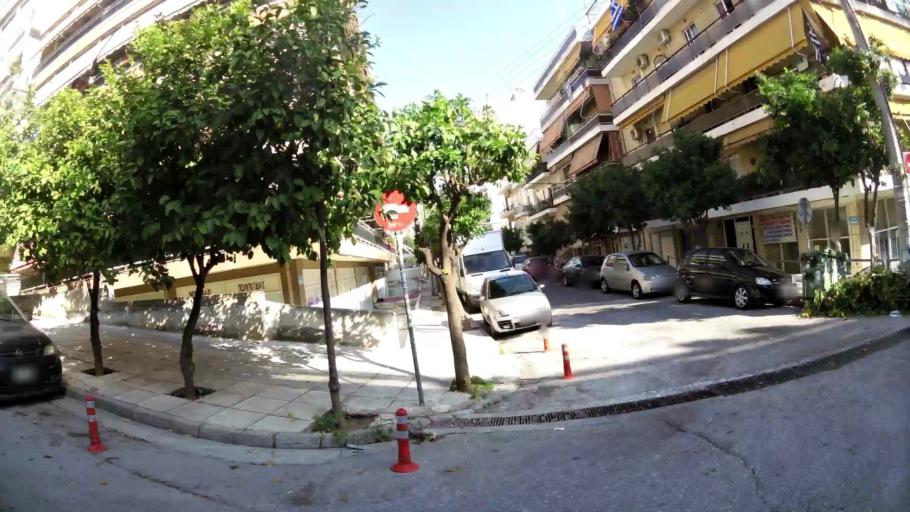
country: GR
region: Attica
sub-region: Nomos Piraios
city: Keratsini
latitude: 37.9648
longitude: 23.6322
